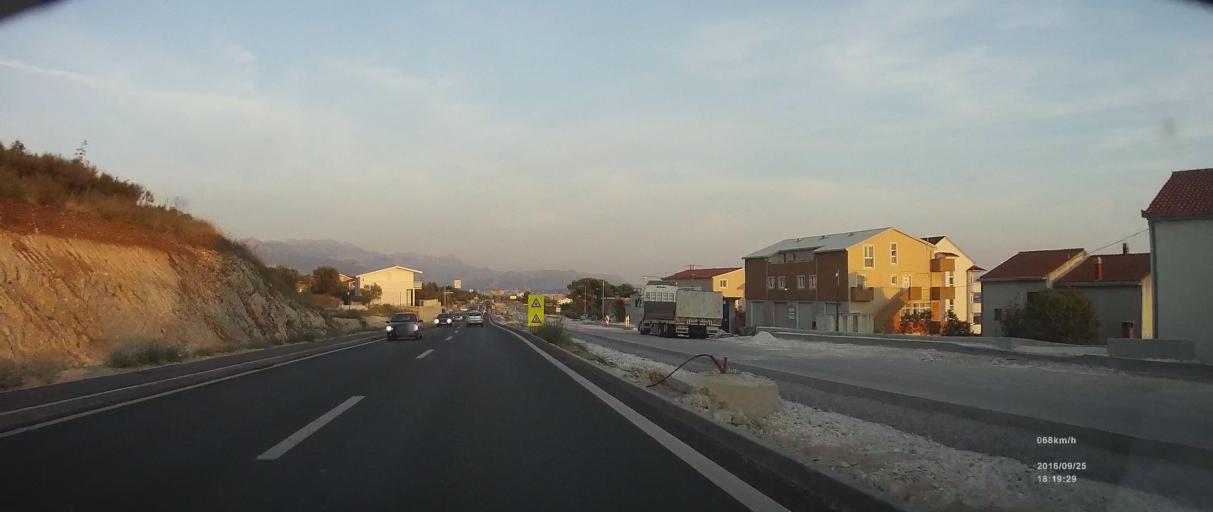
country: HR
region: Splitsko-Dalmatinska
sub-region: Grad Split
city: Split
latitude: 43.5547
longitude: 16.3998
